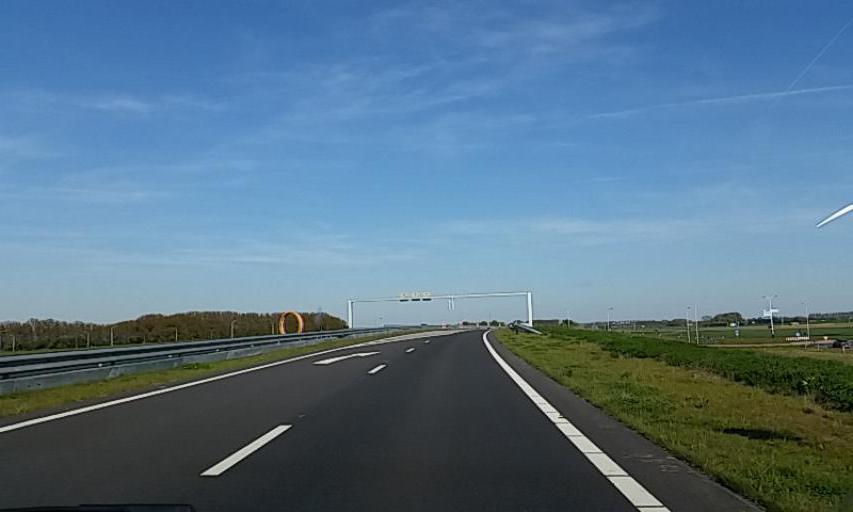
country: NL
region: Zeeland
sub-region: Gemeente Terneuzen
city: Sluiskil
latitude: 51.2946
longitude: 3.8591
